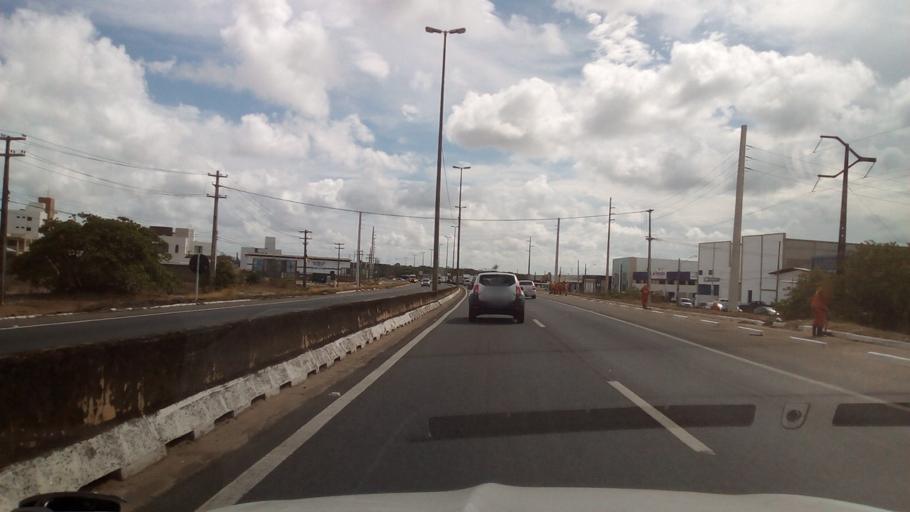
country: BR
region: Paraiba
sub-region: Joao Pessoa
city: Joao Pessoa
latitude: -7.0487
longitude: -34.8488
